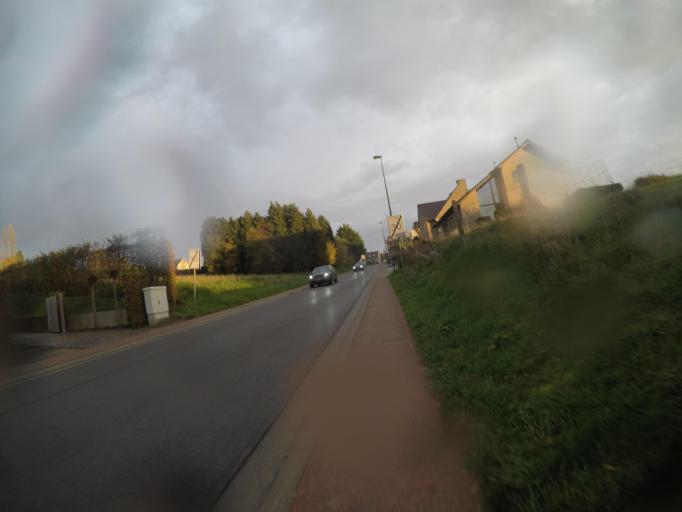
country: BE
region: Flanders
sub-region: Provincie Vlaams-Brabant
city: Ternat
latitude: 50.8480
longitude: 4.1384
